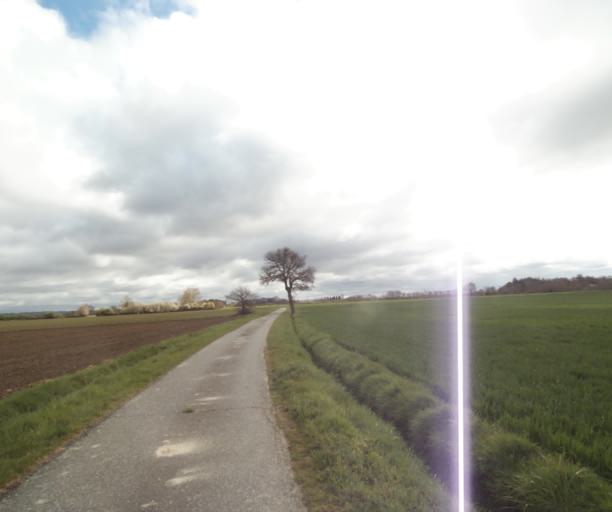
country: FR
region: Midi-Pyrenees
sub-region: Departement de l'Ariege
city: Saverdun
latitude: 43.2461
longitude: 1.5513
